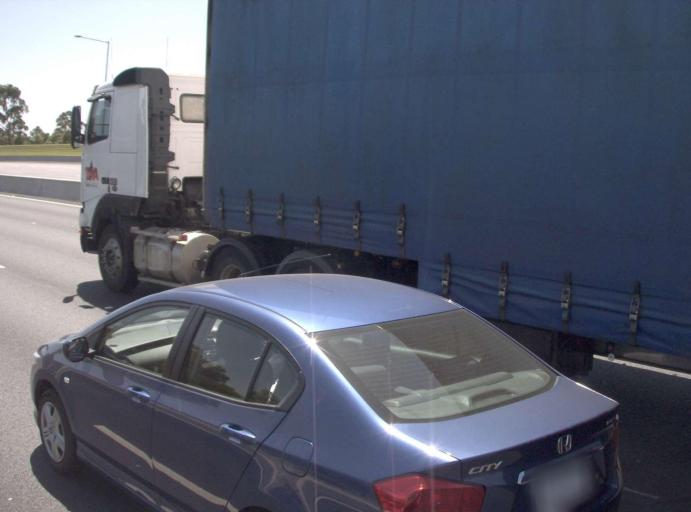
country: AU
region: Victoria
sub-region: Brimbank
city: Deer Park
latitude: -37.7770
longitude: 144.7939
